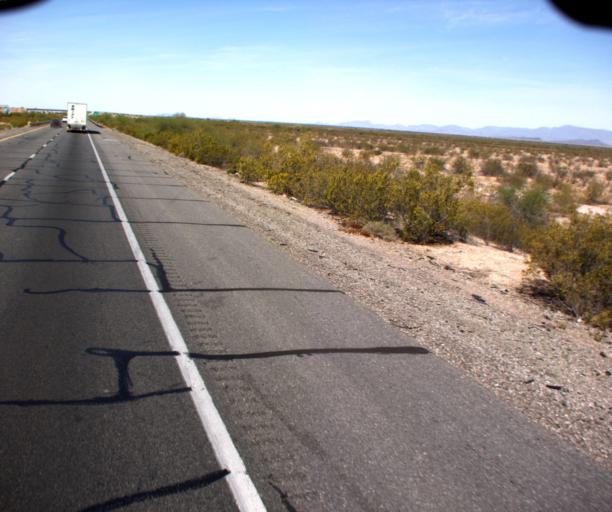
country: US
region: Arizona
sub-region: La Paz County
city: Salome
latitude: 33.5355
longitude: -113.1446
